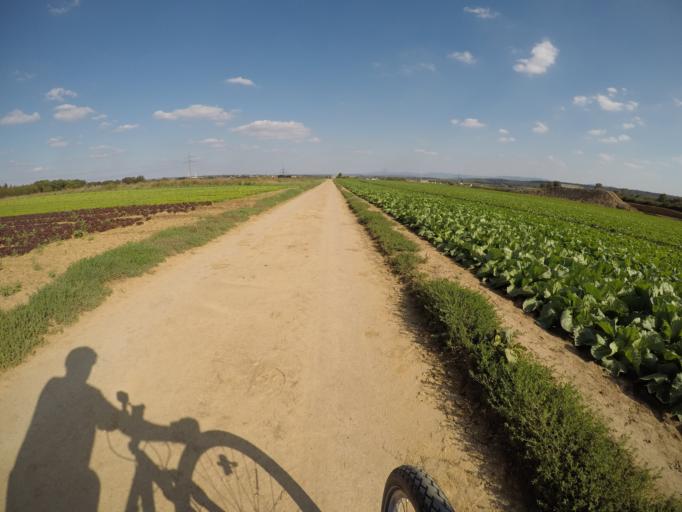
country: DE
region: Baden-Wuerttemberg
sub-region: Regierungsbezirk Stuttgart
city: Neuhausen auf den Fildern
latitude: 48.6958
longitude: 9.2888
